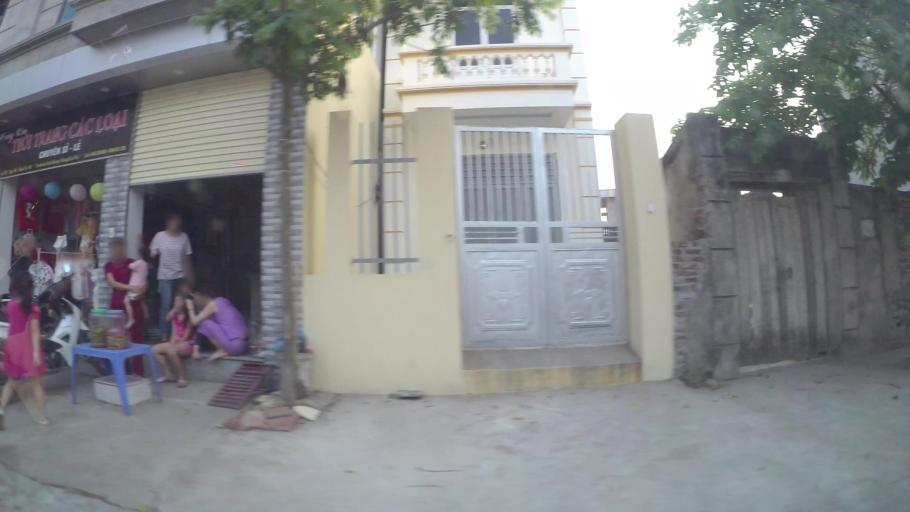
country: VN
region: Ha Noi
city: Van Dien
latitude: 20.9269
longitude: 105.8376
